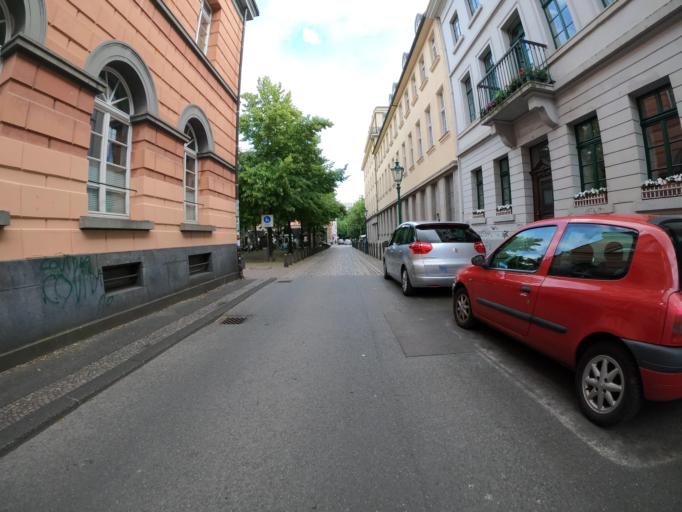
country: DE
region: North Rhine-Westphalia
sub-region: Regierungsbezirk Dusseldorf
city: Wuppertal
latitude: 51.2566
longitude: 7.1390
